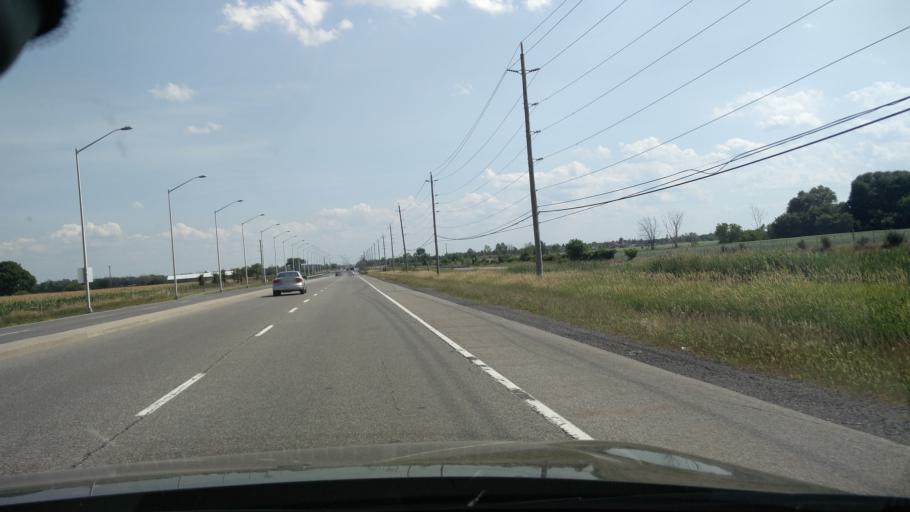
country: CA
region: Ontario
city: Bells Corners
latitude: 45.3093
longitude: -75.7375
